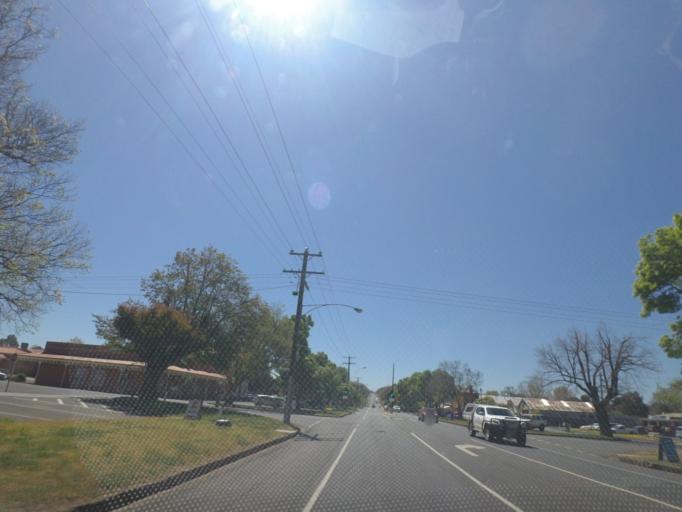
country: AU
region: Victoria
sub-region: Hume
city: Sunbury
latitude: -37.3492
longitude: 144.7427
